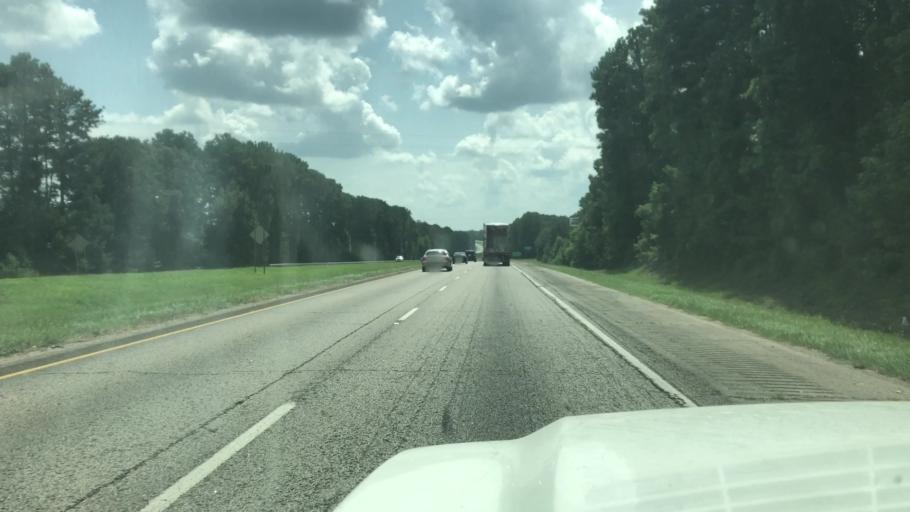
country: US
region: Georgia
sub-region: Troup County
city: La Grange
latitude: 32.9599
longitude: -85.0843
